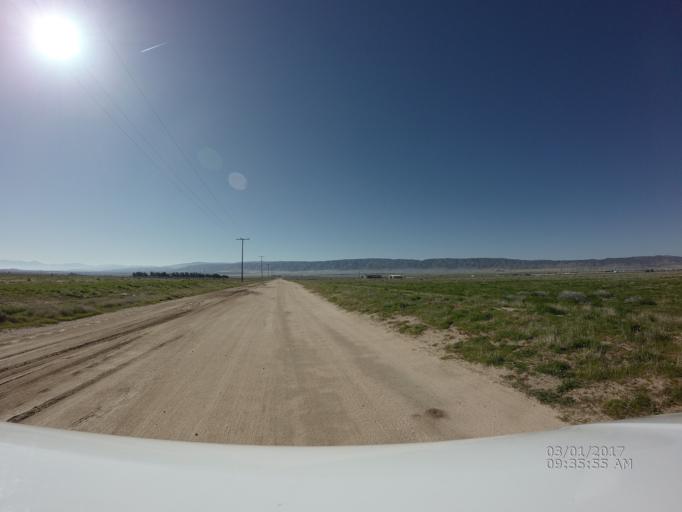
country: US
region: California
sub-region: Los Angeles County
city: Quartz Hill
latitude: 34.7000
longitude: -118.2718
